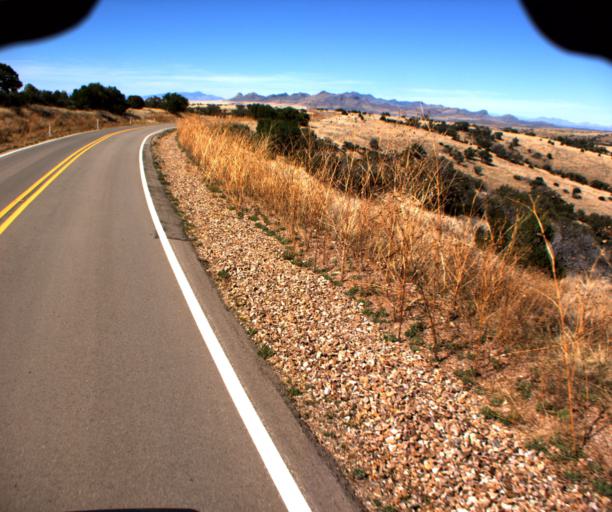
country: US
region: Arizona
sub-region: Cochise County
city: Huachuca City
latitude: 31.5264
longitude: -110.5027
